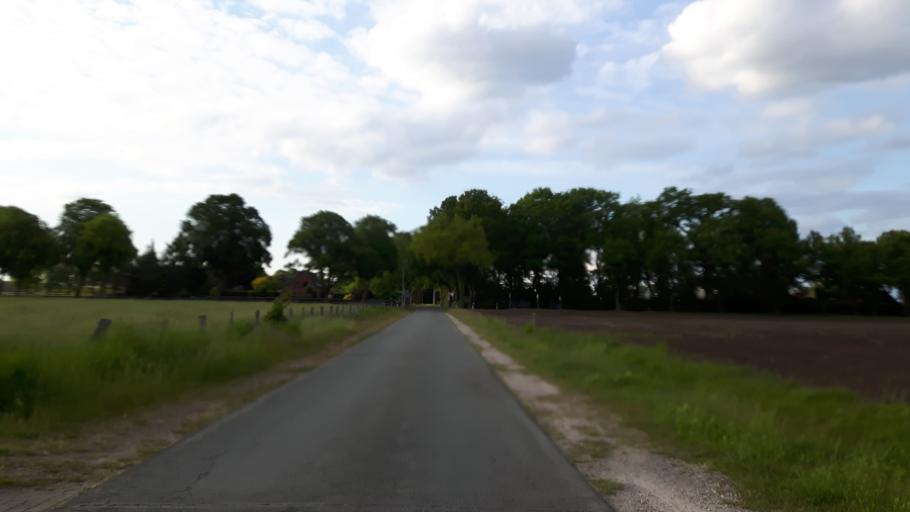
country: DE
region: Lower Saxony
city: Delmenhorst
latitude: 53.0144
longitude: 8.6011
